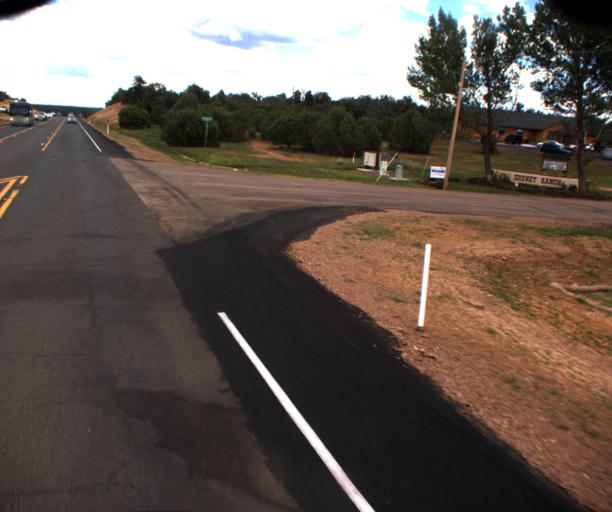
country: US
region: Arizona
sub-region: Navajo County
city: Linden
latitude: 34.2854
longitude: -110.1287
